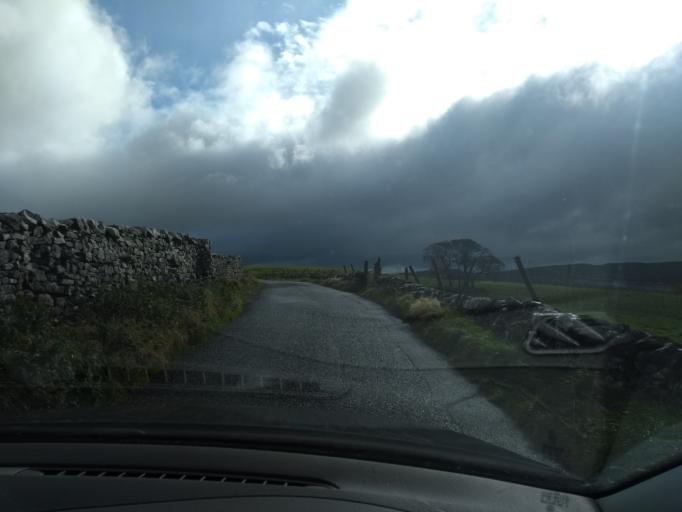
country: GB
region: England
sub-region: North Yorkshire
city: Settle
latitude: 54.1039
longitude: -2.2267
